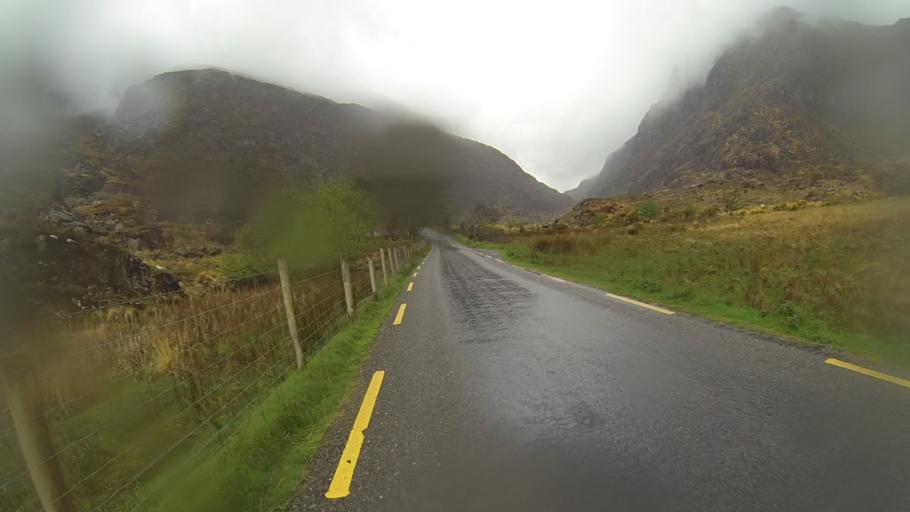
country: IE
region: Munster
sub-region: Ciarrai
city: Cill Airne
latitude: 52.0175
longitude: -9.6358
